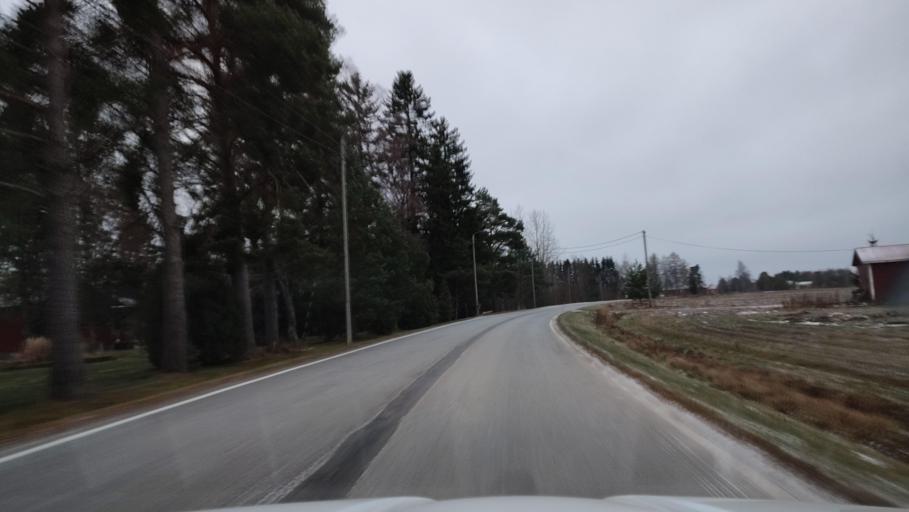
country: FI
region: Southern Ostrobothnia
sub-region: Suupohja
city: Karijoki
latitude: 62.2461
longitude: 21.6708
